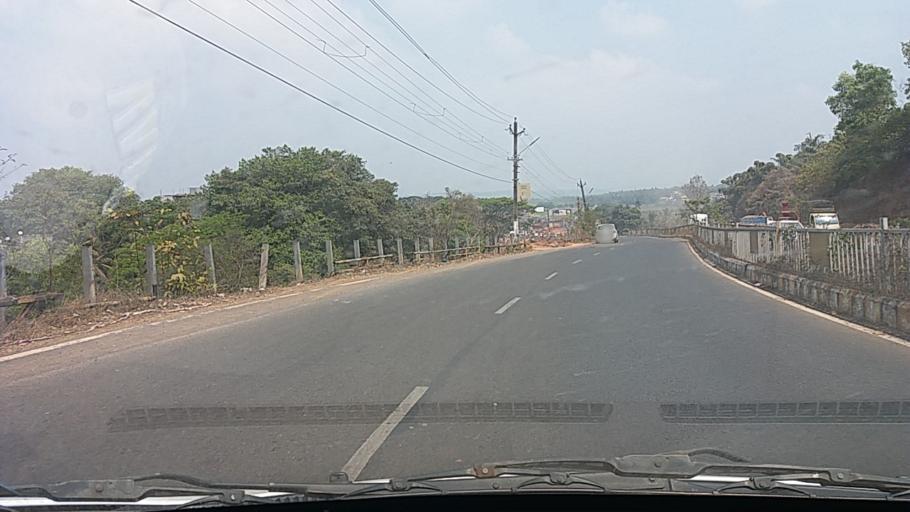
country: IN
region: Goa
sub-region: North Goa
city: Bambolim
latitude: 15.4674
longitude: 73.8510
